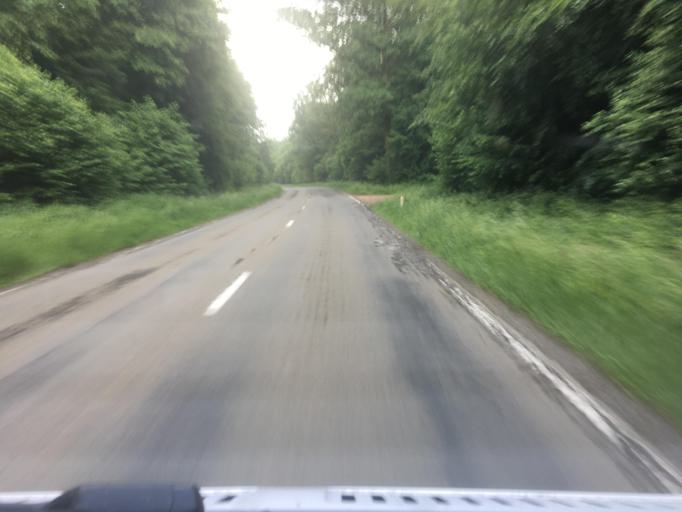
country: BE
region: Wallonia
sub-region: Province du Luxembourg
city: Florenville
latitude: 49.6803
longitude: 5.3347
